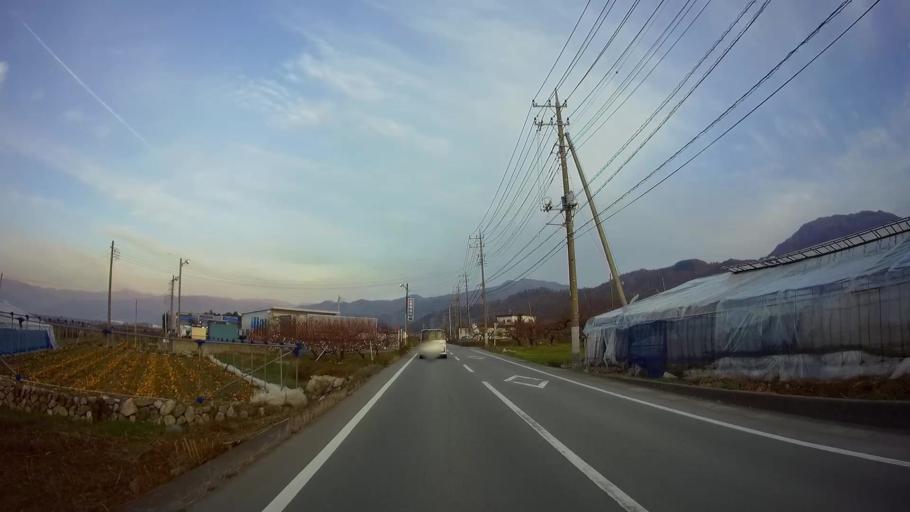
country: JP
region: Yamanashi
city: Isawa
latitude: 35.6121
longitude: 138.6574
